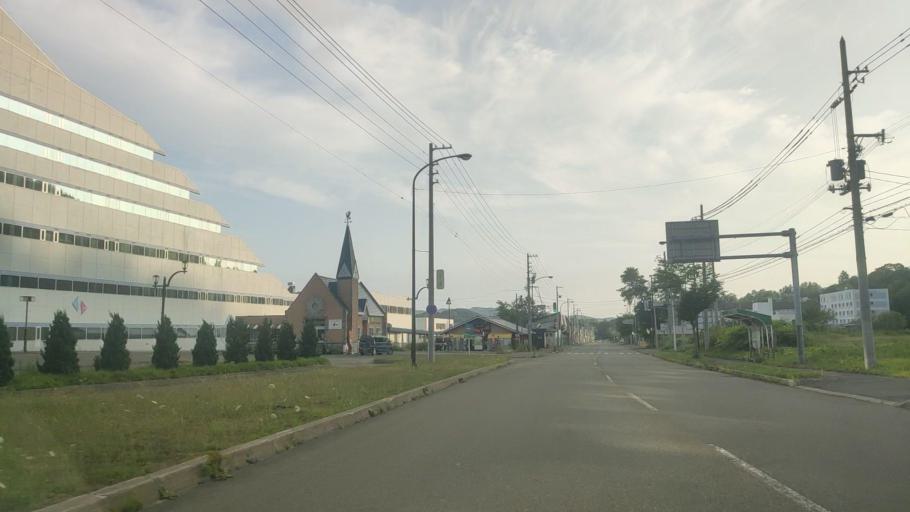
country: JP
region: Hokkaido
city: Iwamizawa
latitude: 43.0515
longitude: 141.9675
